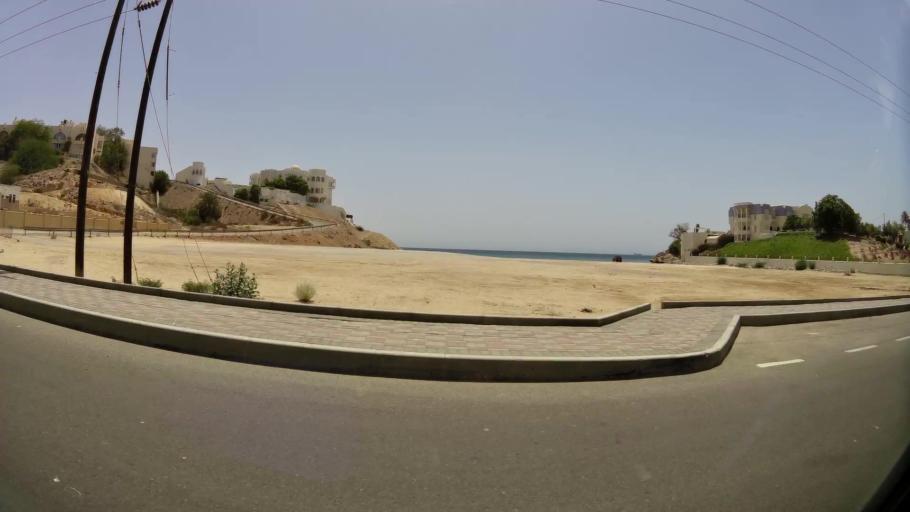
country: OM
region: Muhafazat Masqat
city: Muscat
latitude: 23.6342
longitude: 58.4879
